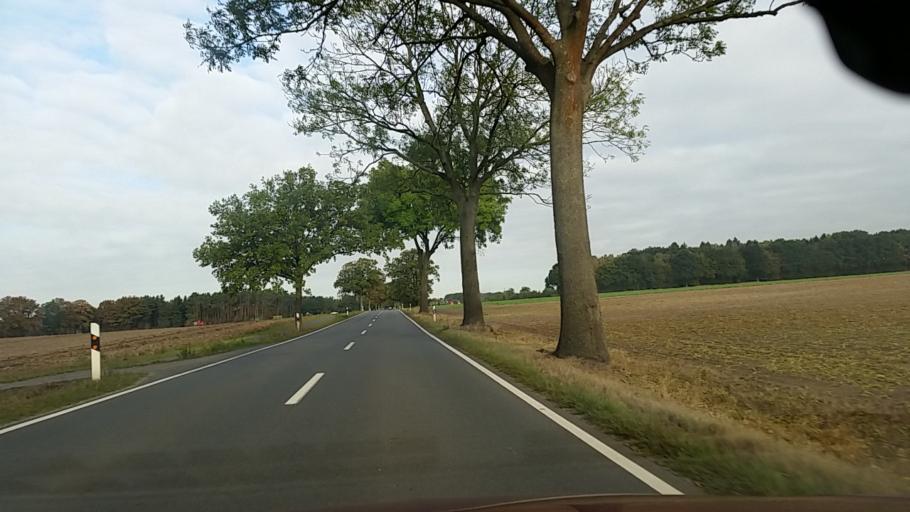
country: DE
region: Lower Saxony
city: Ahnsbeck
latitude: 52.5982
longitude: 10.3083
